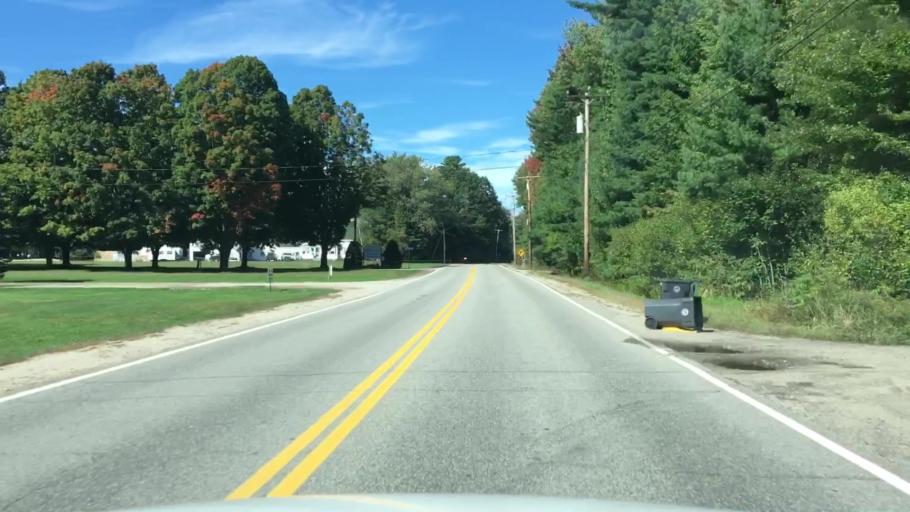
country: US
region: Maine
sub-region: Cumberland County
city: Westbrook
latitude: 43.6464
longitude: -70.3982
